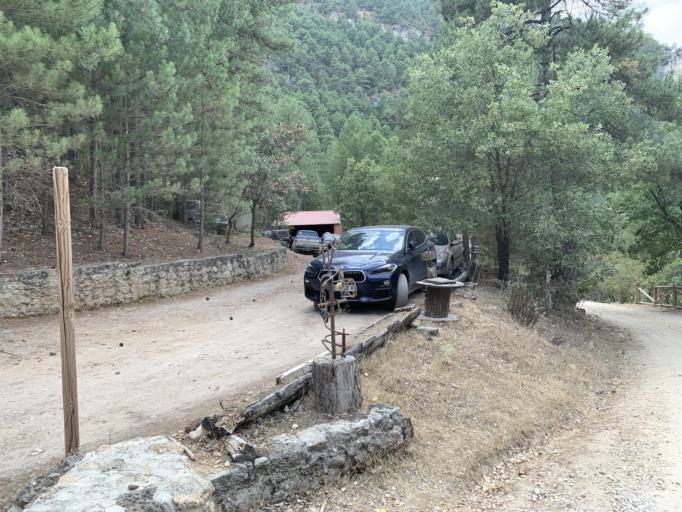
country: ES
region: Castille-La Mancha
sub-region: Provincia de Guadalajara
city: Taravilla
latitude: 40.6485
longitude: -1.9785
